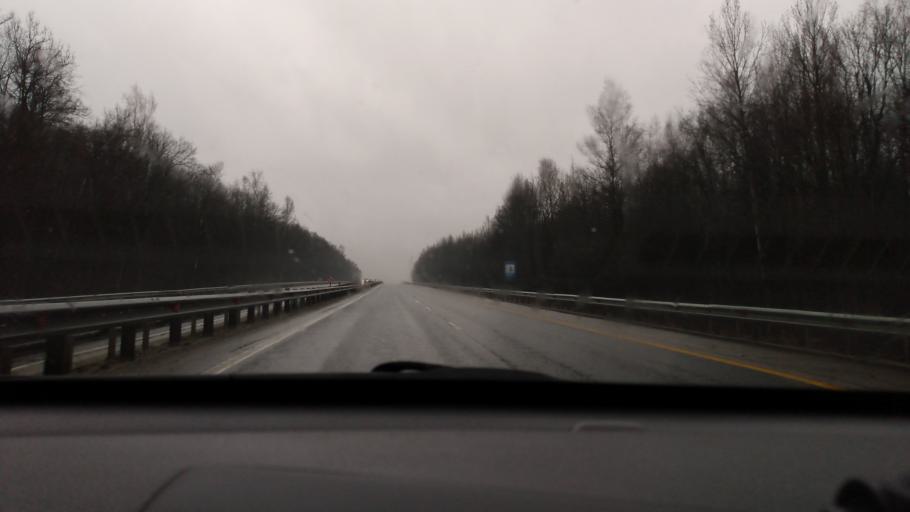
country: RU
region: Tula
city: Venev
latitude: 54.3557
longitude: 38.1547
